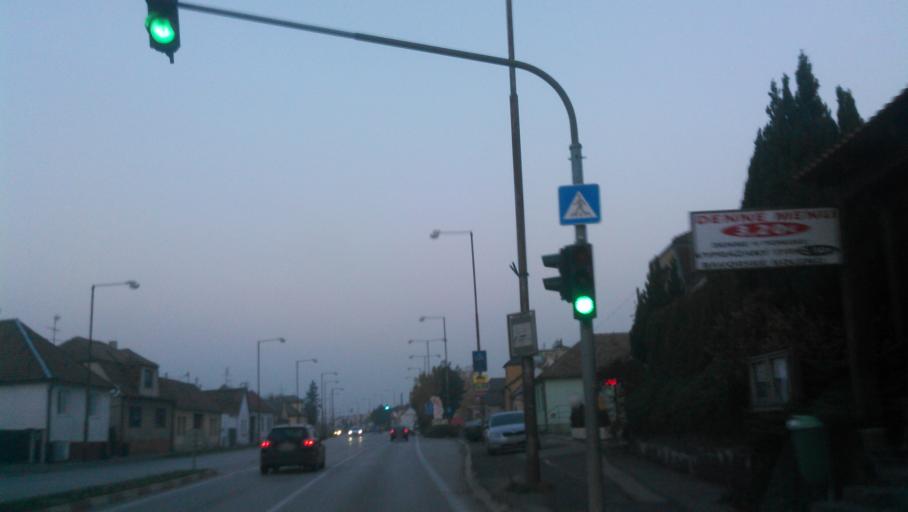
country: SK
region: Bratislavsky
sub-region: Okres Pezinok
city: Pezinok
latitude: 48.2711
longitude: 17.2494
